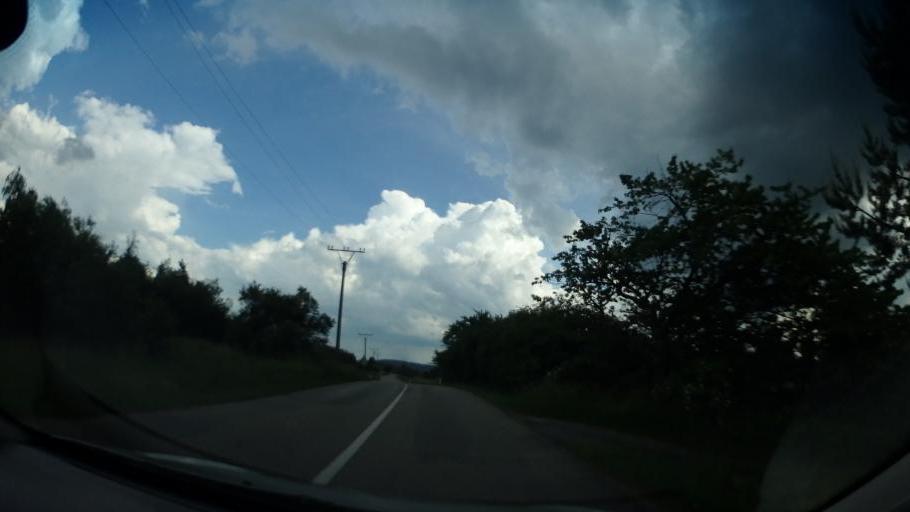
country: CZ
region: South Moravian
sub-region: Okres Brno-Venkov
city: Dolni Loucky
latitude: 49.4016
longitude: 16.3248
